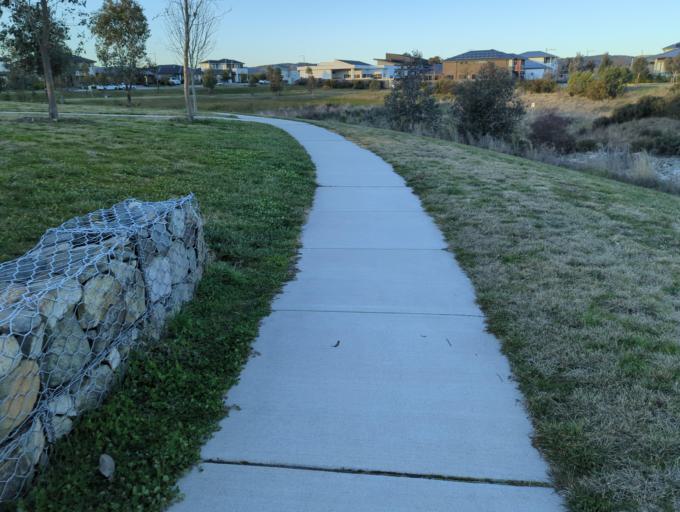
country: AU
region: New South Wales
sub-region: Queanbeyan
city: Queanbeyan
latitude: -35.4247
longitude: 149.2459
